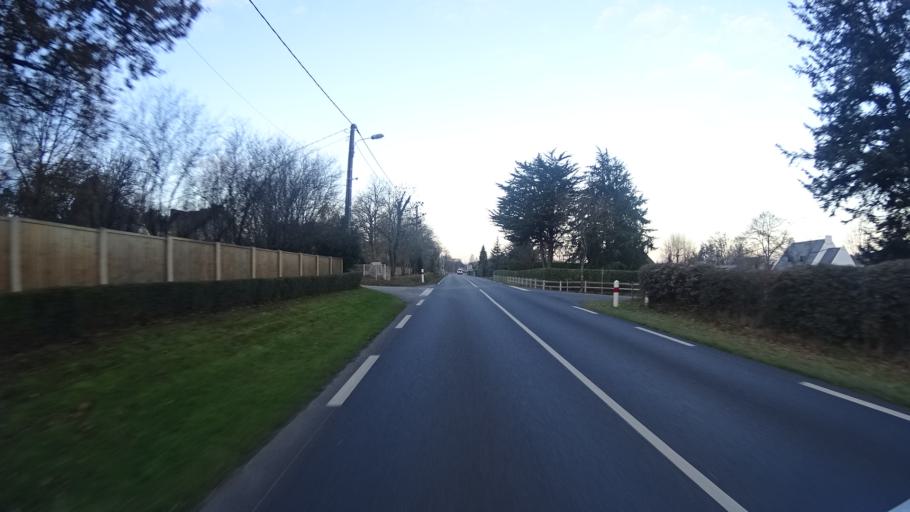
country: FR
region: Pays de la Loire
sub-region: Departement de la Loire-Atlantique
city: Saint-Nicolas-de-Redon
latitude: 47.6427
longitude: -2.0435
